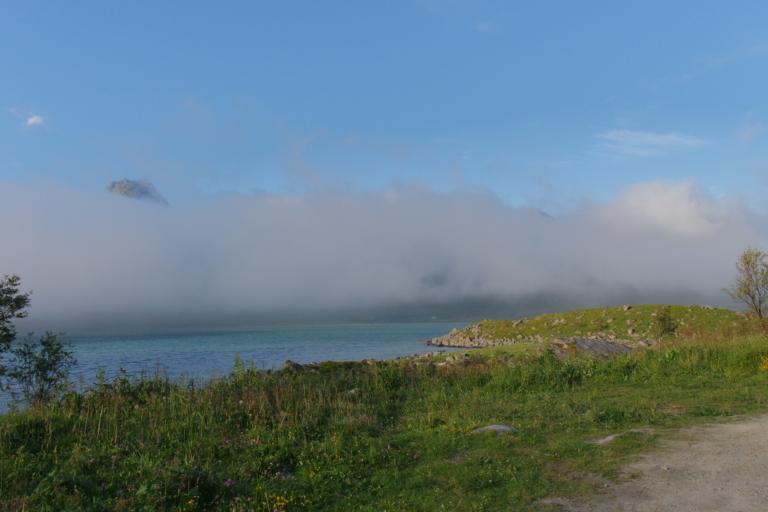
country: NO
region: Nordland
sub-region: Flakstad
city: Ramberg
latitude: 68.0771
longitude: 13.3121
